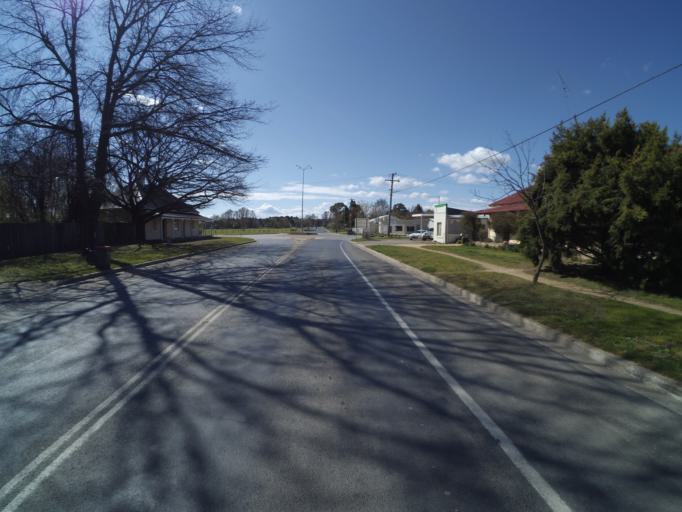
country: AU
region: New South Wales
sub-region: Palerang
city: Bungendore
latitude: -35.2544
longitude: 149.4382
